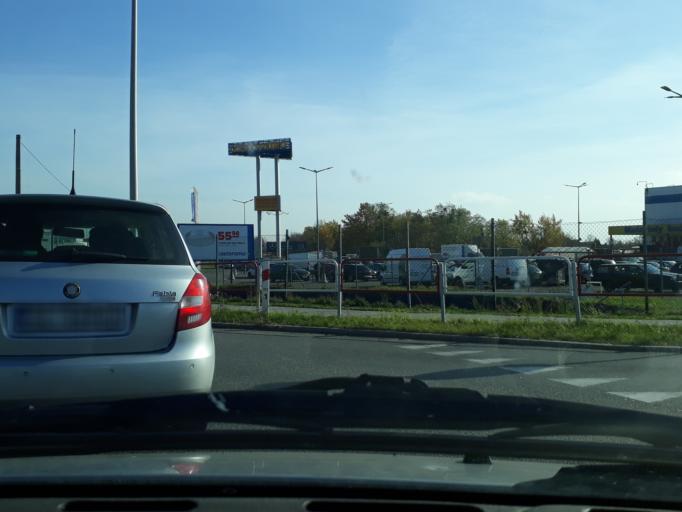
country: PL
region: Silesian Voivodeship
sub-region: Powiat tarnogorski
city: Tarnowskie Gory
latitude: 50.4376
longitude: 18.8421
